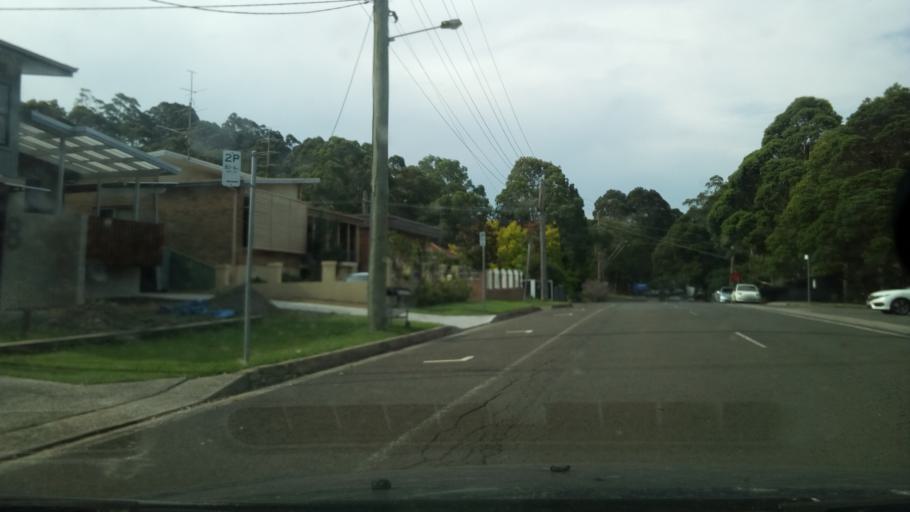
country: AU
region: New South Wales
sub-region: Wollongong
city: Mount Ousley
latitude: -34.4082
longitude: 150.8716
